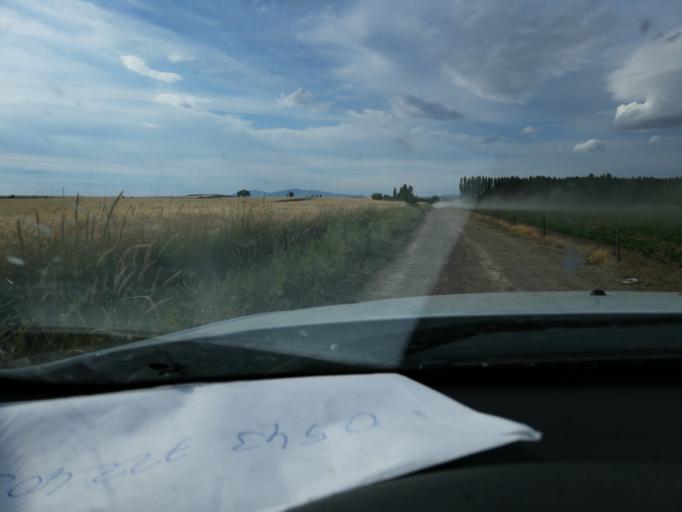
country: TR
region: Kirsehir
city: Kirsehir
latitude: 38.9999
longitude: 34.1244
